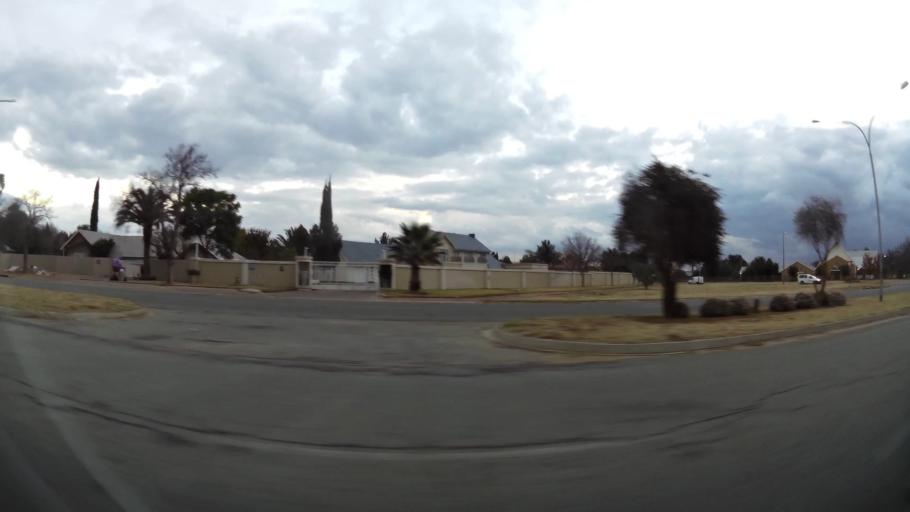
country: ZA
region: Orange Free State
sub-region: Lejweleputswa District Municipality
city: Welkom
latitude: -27.9674
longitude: 26.7272
